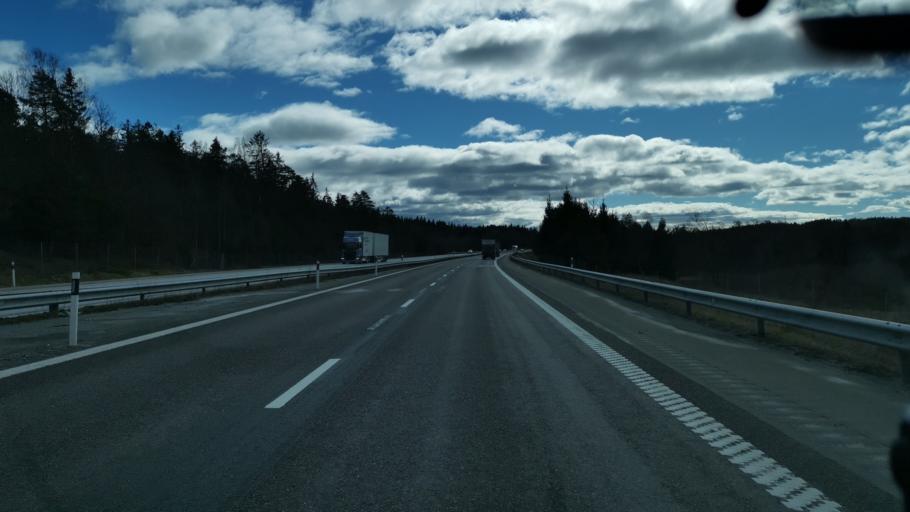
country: SE
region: Vaestra Goetaland
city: Svanesund
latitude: 58.1363
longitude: 11.8855
